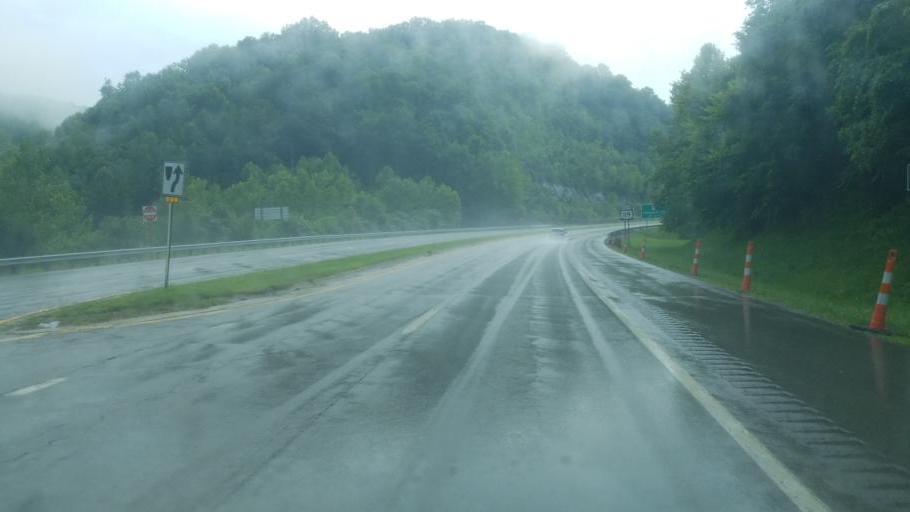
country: US
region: West Virginia
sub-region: Logan County
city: Chapmanville
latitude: 37.9746
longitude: -81.9971
